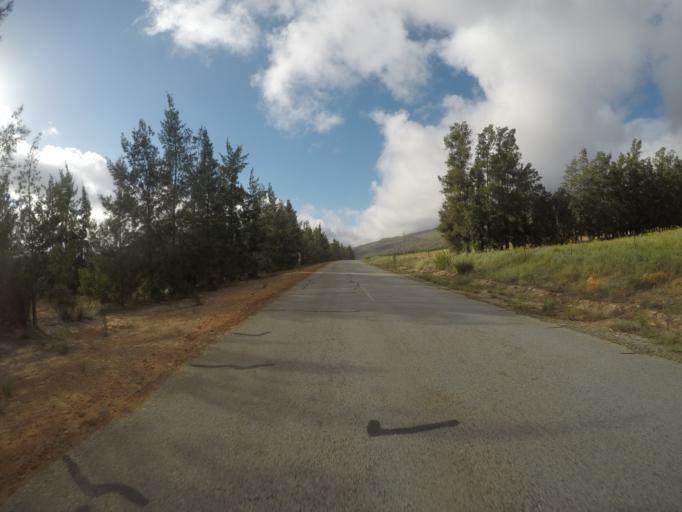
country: ZA
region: Western Cape
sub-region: West Coast District Municipality
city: Clanwilliam
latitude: -32.3500
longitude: 18.8473
